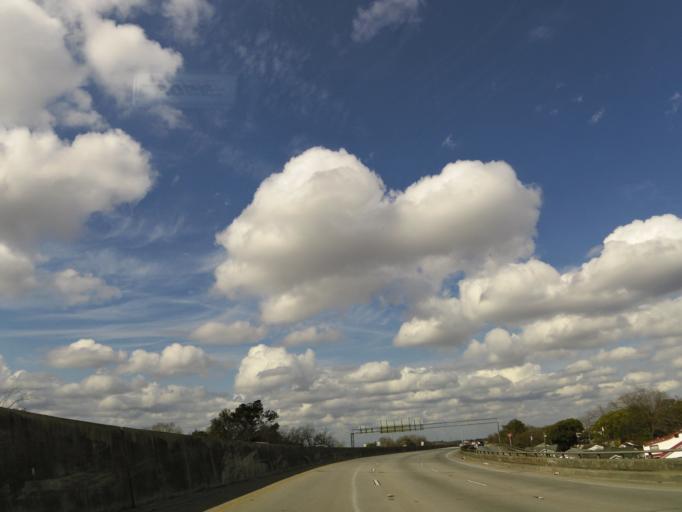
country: US
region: South Carolina
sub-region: Charleston County
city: Charleston
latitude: 32.8130
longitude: -79.9534
